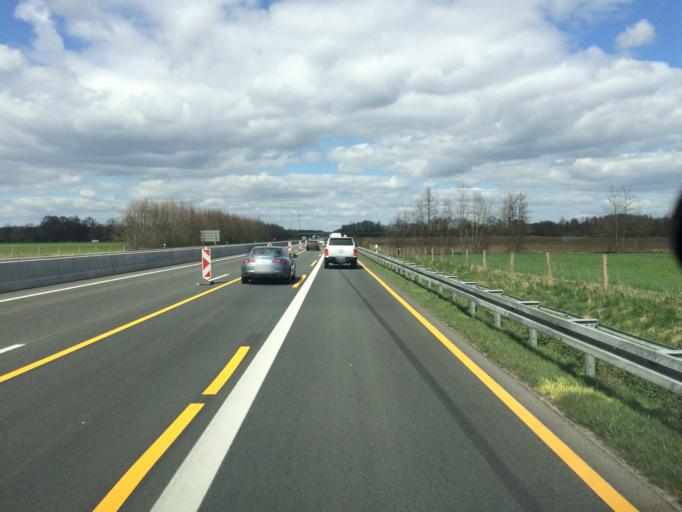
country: DE
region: North Rhine-Westphalia
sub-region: Regierungsbezirk Munster
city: Gescher
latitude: 51.9492
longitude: 7.0460
